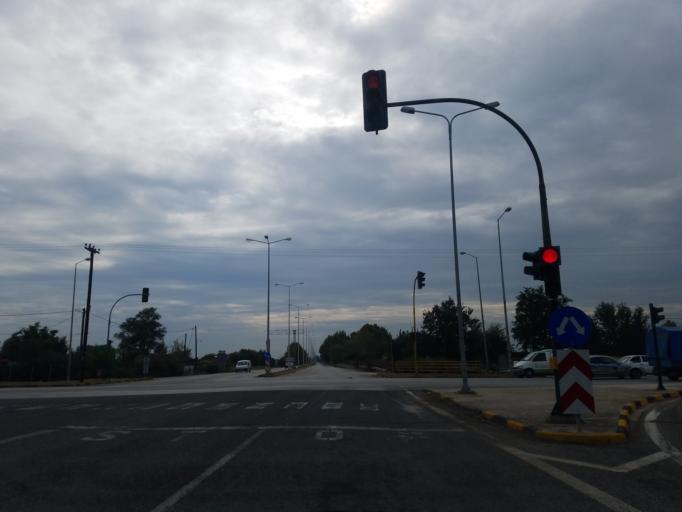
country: GR
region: Thessaly
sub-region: Trikala
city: Pyrgetos
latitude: 39.5298
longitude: 21.7441
